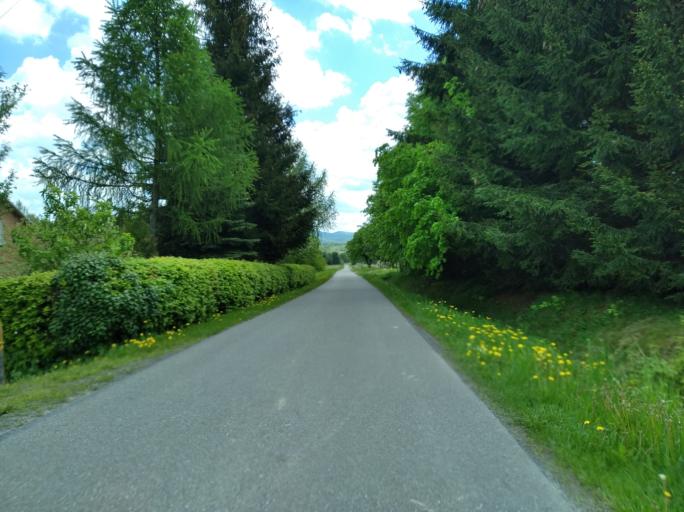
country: PL
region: Subcarpathian Voivodeship
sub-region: Powiat strzyzowski
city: Frysztak
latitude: 49.8334
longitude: 21.5763
